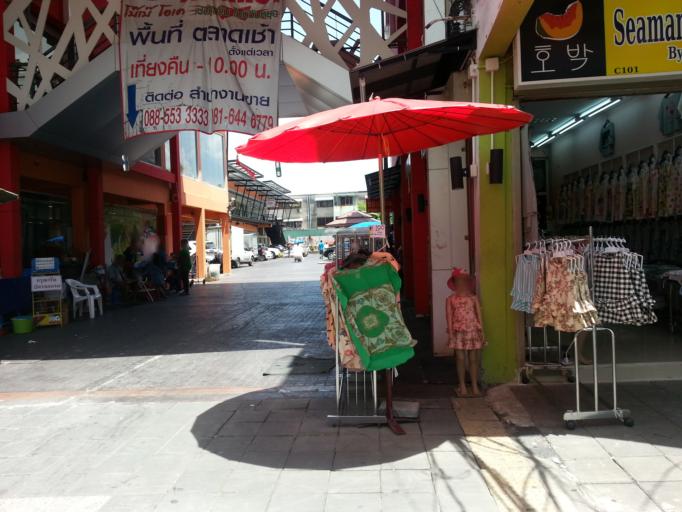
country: TH
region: Bangkok
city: Pom Prap Sattru Phai
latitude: 13.7547
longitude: 100.5145
